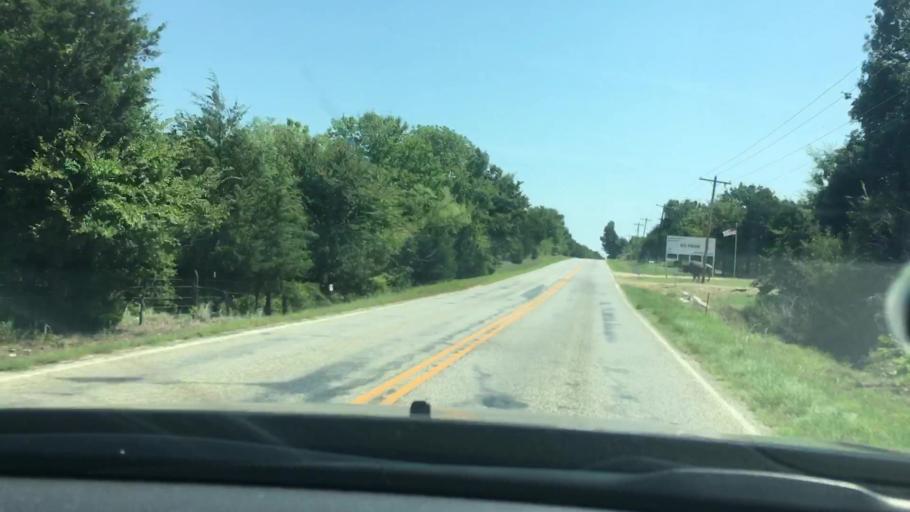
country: US
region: Oklahoma
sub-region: Johnston County
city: Tishomingo
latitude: 34.2377
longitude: -96.5727
